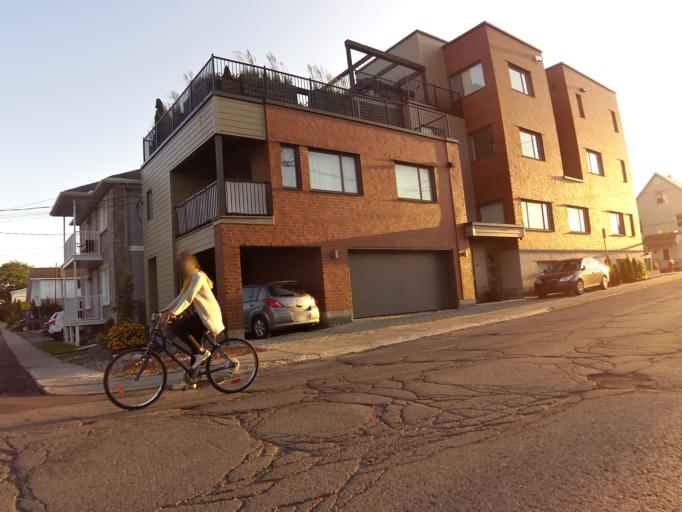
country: CA
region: Ontario
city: Ottawa
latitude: 45.4337
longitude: -75.7185
